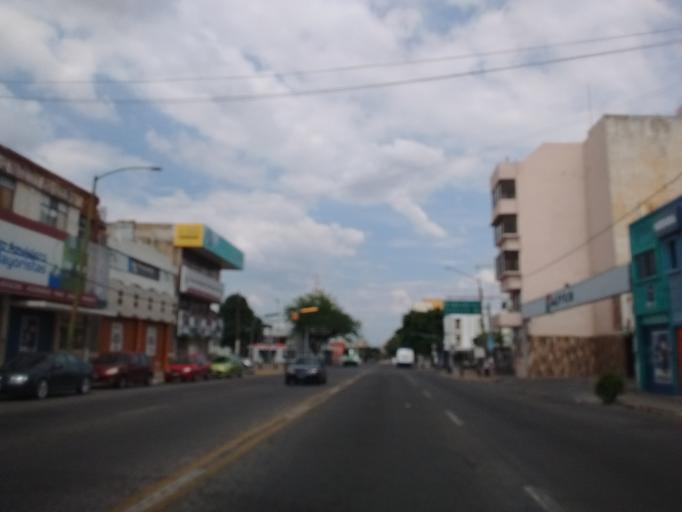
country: MX
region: Jalisco
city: Guadalajara
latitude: 20.6659
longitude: -103.3564
